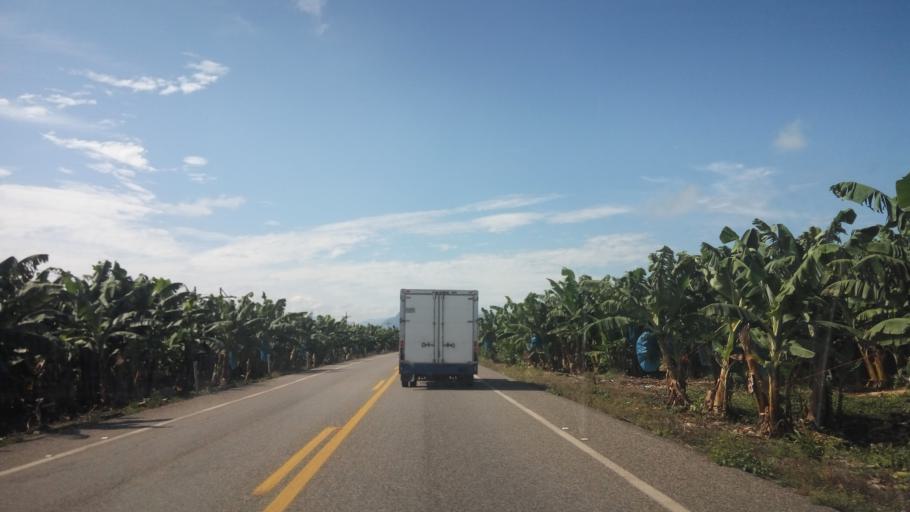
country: MX
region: Tabasco
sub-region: Teapa
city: Eureka y Belen
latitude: 17.6460
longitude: -92.9653
